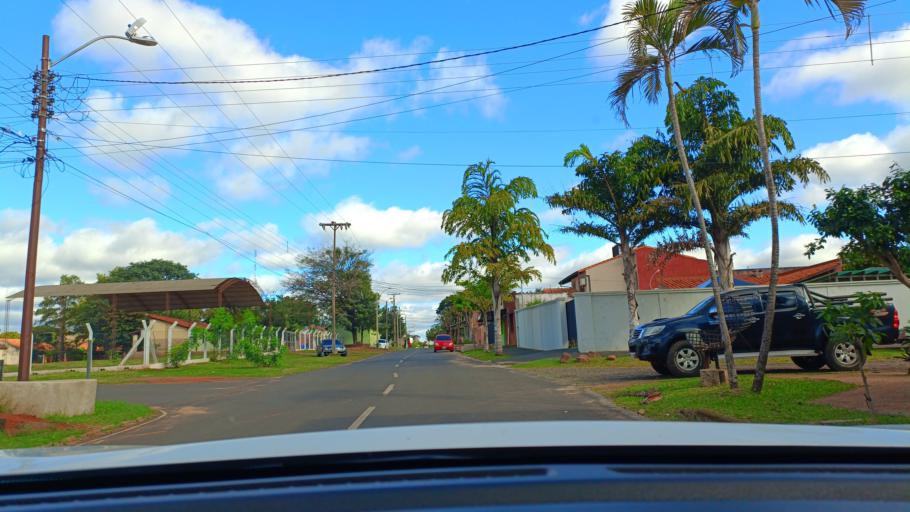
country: PY
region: San Pedro
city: Guayaybi
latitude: -24.6595
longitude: -56.4436
